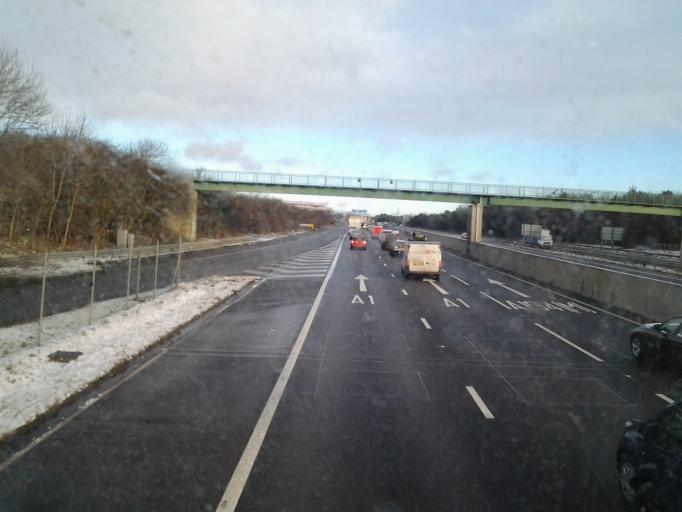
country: GB
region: England
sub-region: County Durham
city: Chester-le-Street
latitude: 54.8908
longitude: -1.5594
